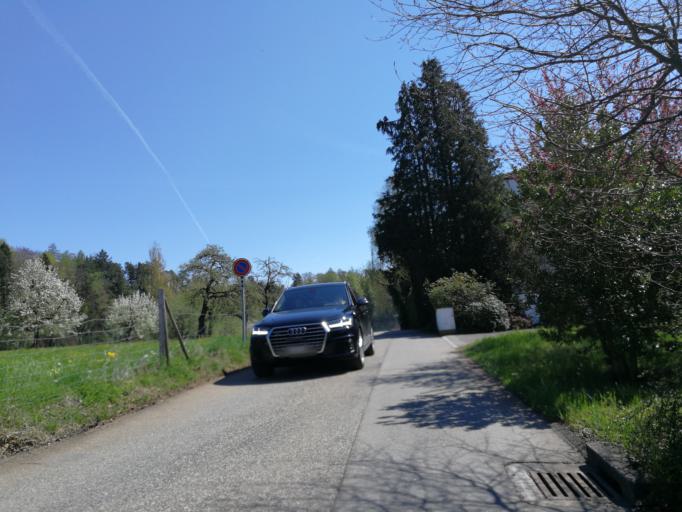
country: CH
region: Zurich
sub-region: Bezirk Meilen
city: Mannedorf
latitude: 47.2608
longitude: 8.7109
